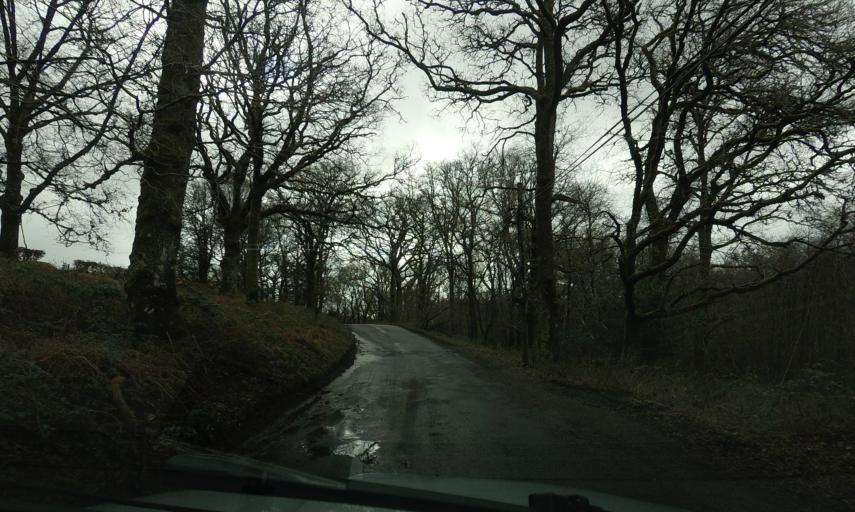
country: GB
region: Scotland
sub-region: West Dunbartonshire
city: Balloch
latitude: 56.1051
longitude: -4.5682
